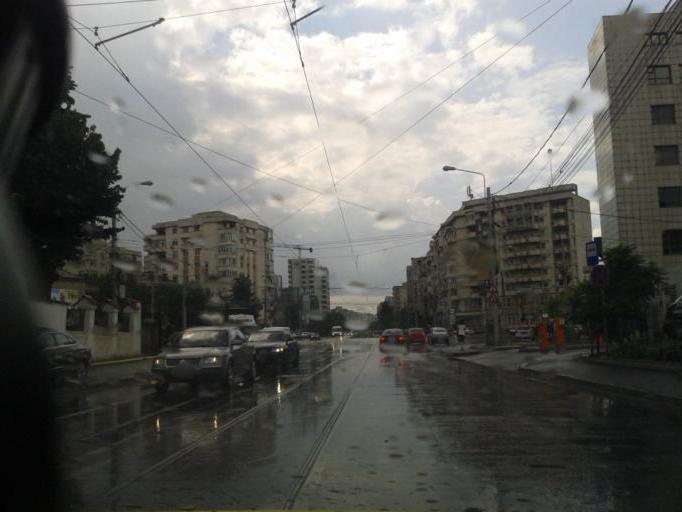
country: RO
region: Prahova
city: Ploiesti
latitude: 44.9455
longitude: 26.0202
